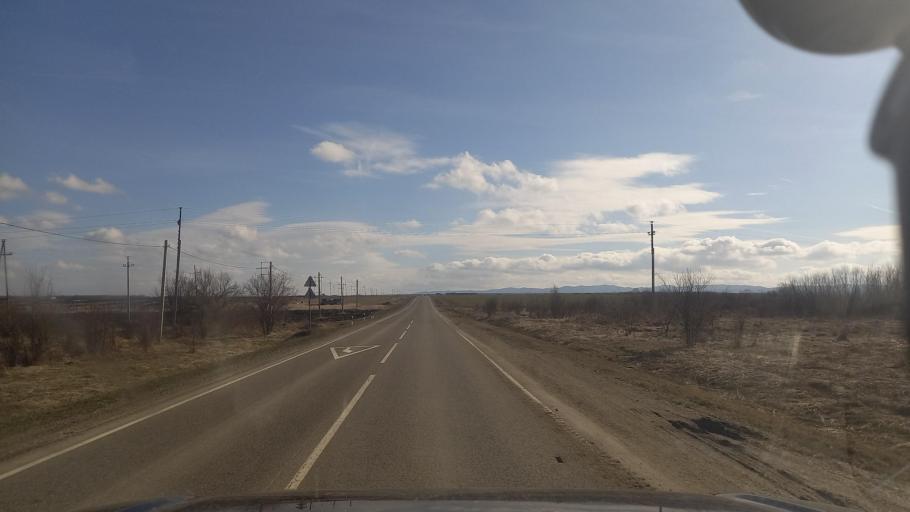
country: RU
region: Krasnodarskiy
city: Novodmitriyevskaya
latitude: 44.8240
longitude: 38.8962
